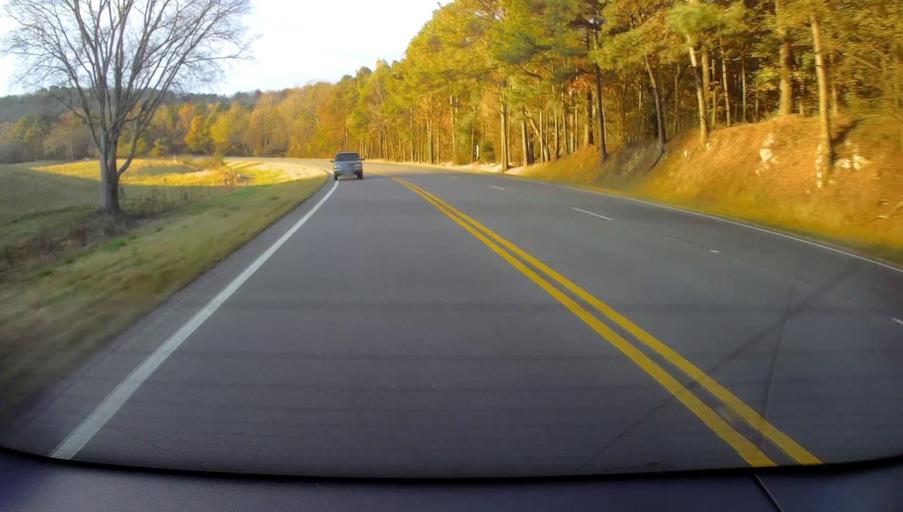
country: US
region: Alabama
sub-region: Etowah County
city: Attalla
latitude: 34.0512
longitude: -86.1609
